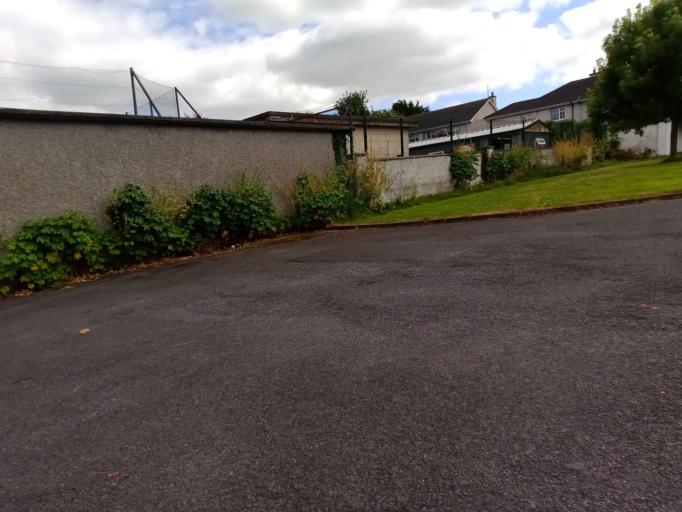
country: IE
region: Leinster
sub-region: Kilkenny
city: Callan
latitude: 52.5444
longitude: -7.3928
